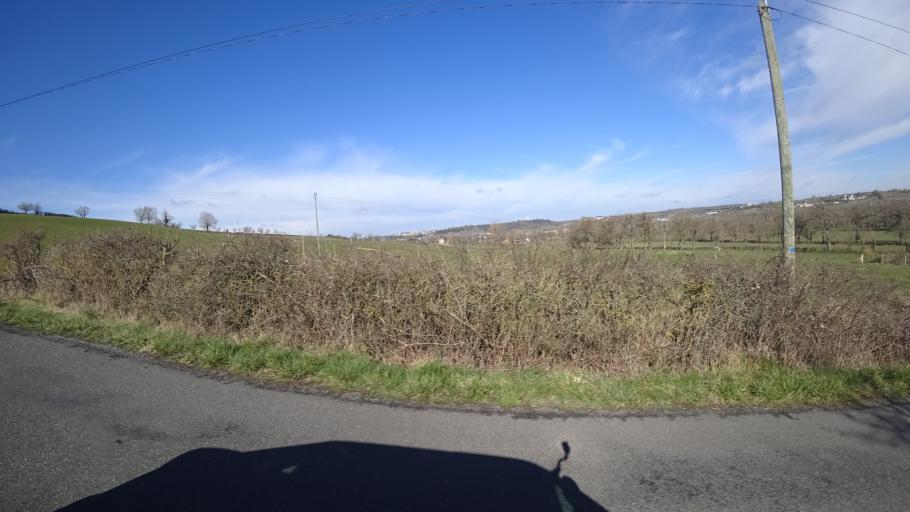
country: FR
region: Midi-Pyrenees
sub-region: Departement de l'Aveyron
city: Rodez
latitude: 44.3683
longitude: 2.6050
